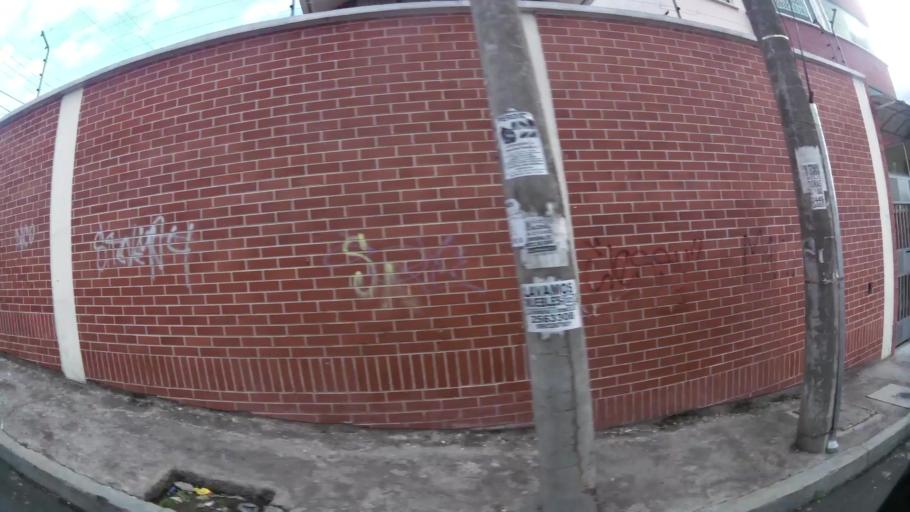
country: EC
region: Pichincha
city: Quito
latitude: -0.1333
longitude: -78.4644
